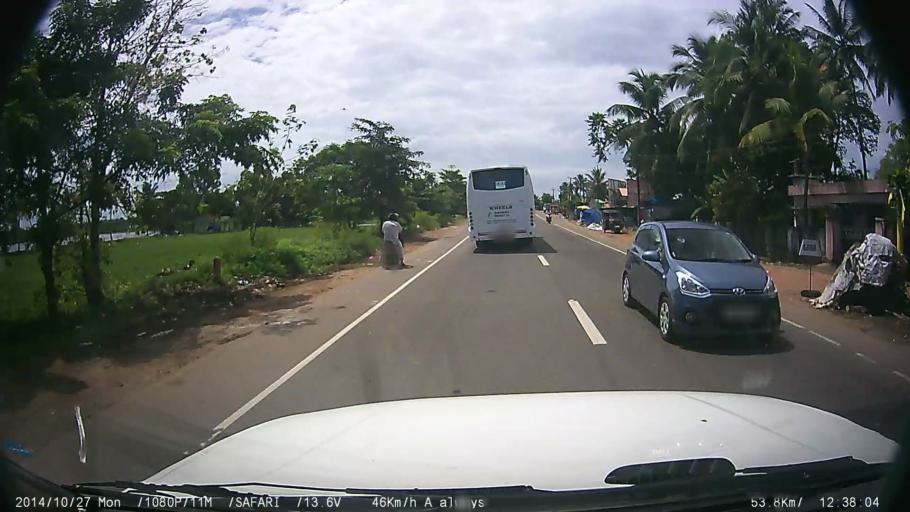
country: IN
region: Kerala
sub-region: Kottayam
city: Changanacheri
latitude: 9.4330
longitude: 76.5304
